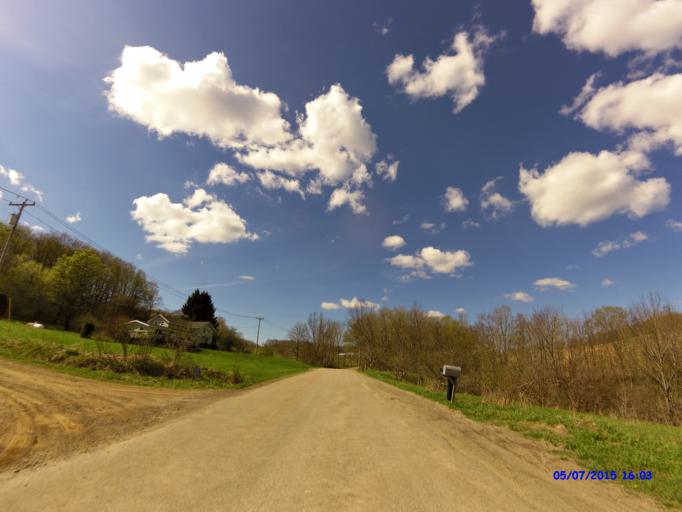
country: US
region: New York
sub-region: Cattaraugus County
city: Franklinville
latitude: 42.2912
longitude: -78.6141
